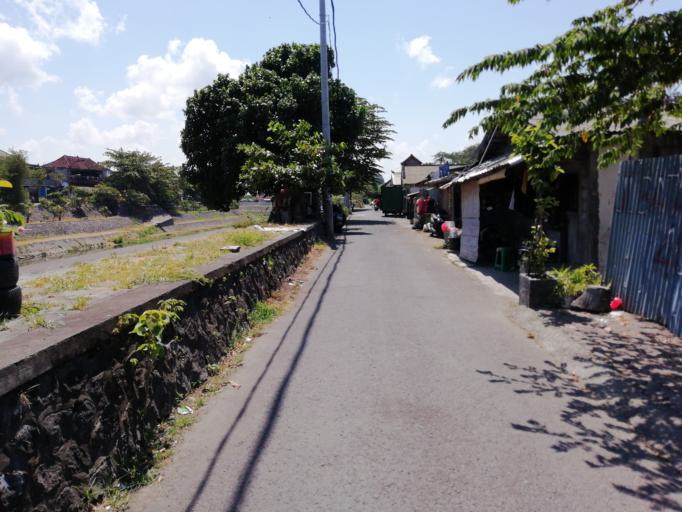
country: ID
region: Bali
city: Karyadharma
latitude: -8.6891
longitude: 115.1984
